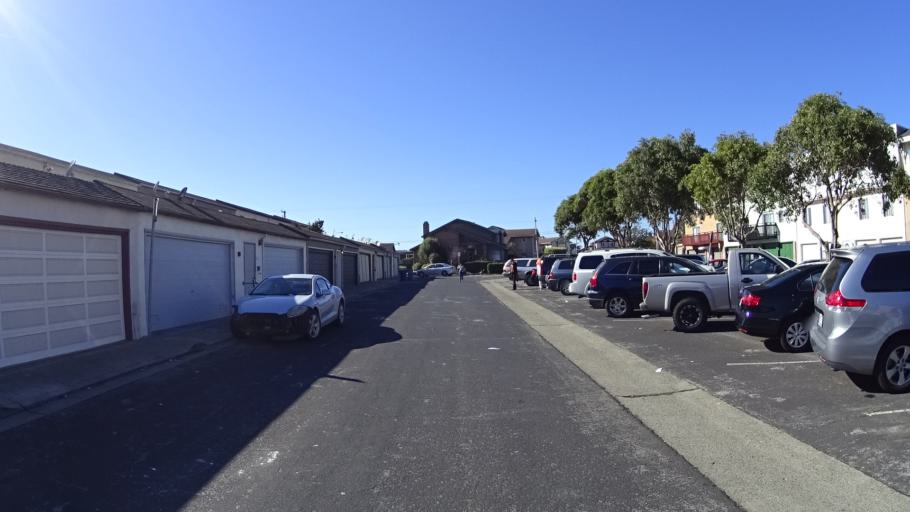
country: US
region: California
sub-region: San Mateo County
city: South San Francisco
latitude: 37.6625
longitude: -122.4317
